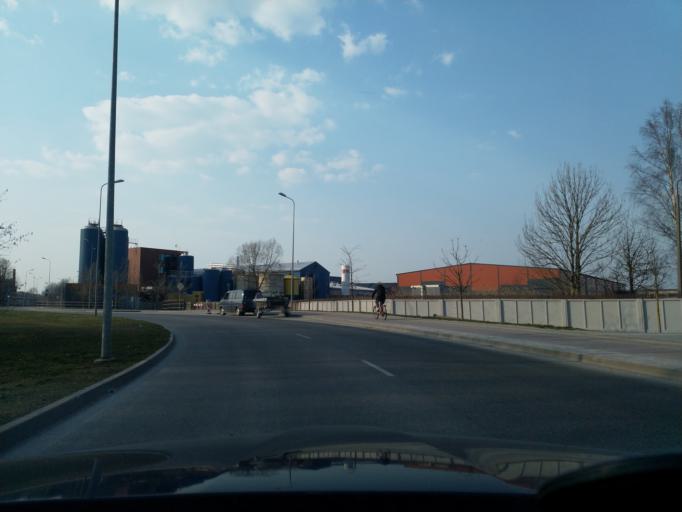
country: LV
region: Liepaja
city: Liepaja
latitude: 56.5094
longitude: 21.0257
